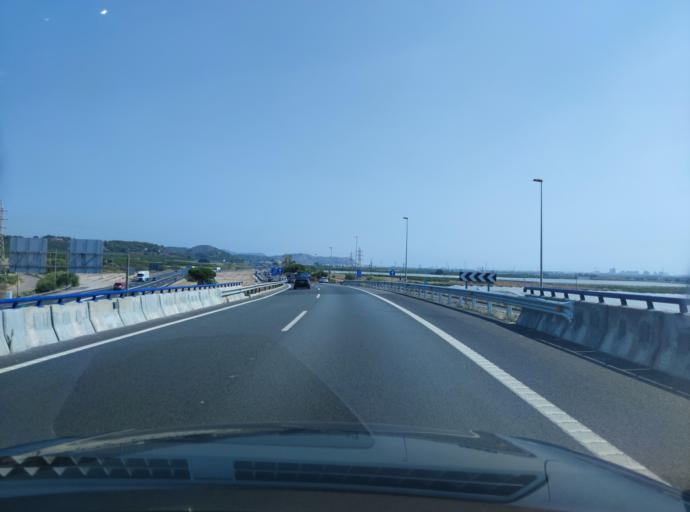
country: ES
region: Valencia
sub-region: Provincia de Valencia
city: Pucol
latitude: 39.6342
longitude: -0.3038
